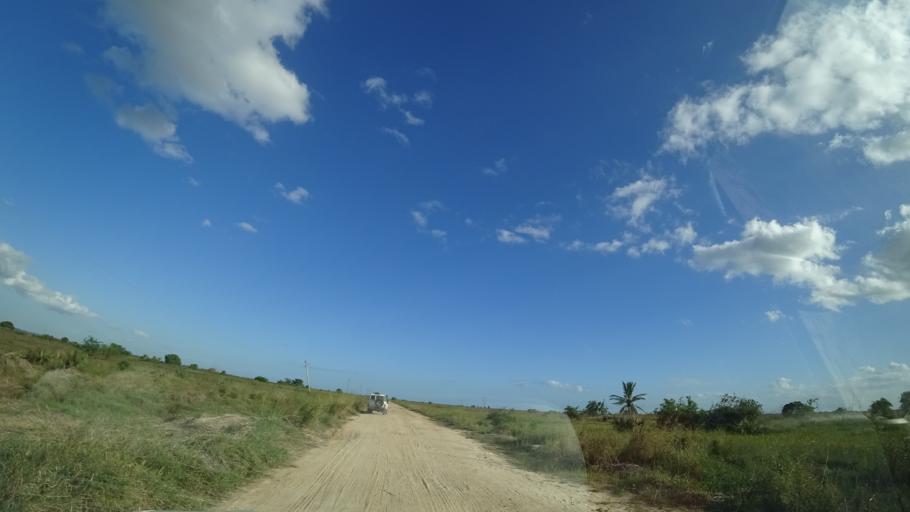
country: MZ
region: Sofala
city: Dondo
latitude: -19.4499
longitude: 34.5625
